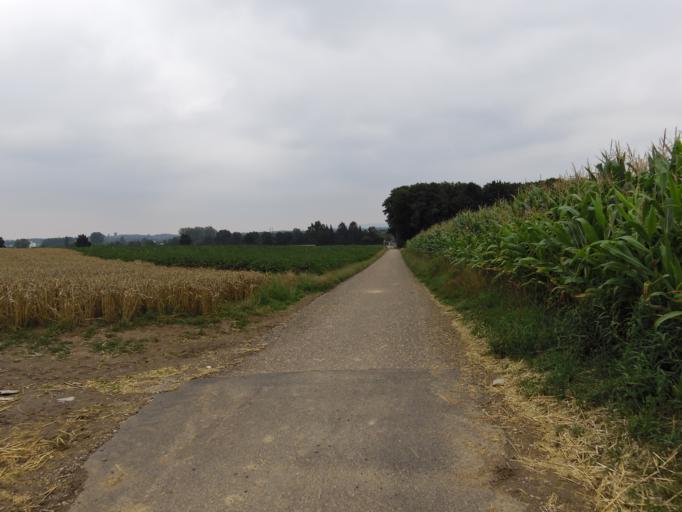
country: DE
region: North Rhine-Westphalia
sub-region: Regierungsbezirk Koln
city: Linnich
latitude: 50.9846
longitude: 6.2552
